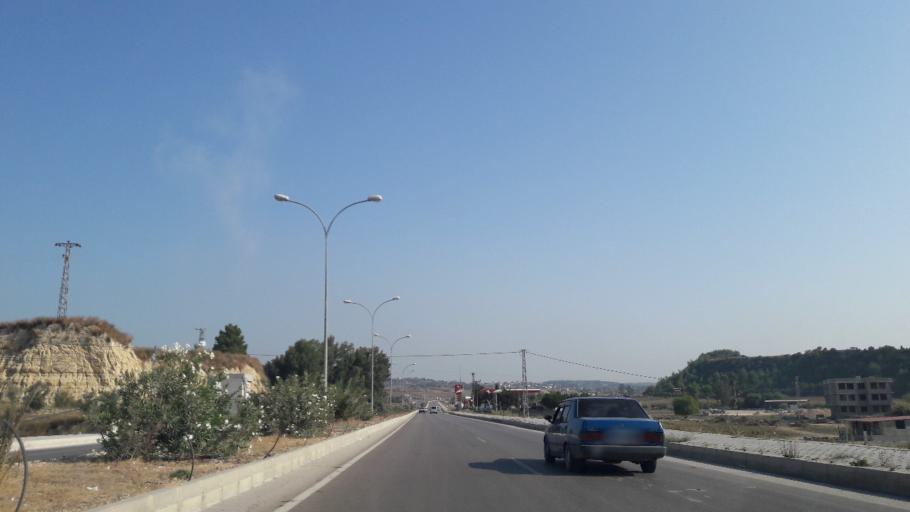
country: TR
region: Adana
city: Yuregir
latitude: 37.0536
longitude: 35.4408
